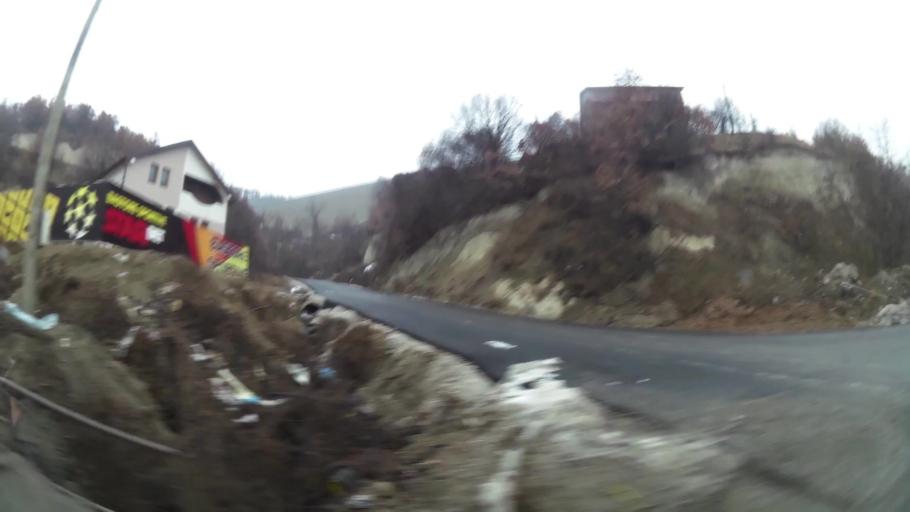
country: XK
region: Ferizaj
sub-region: Hani i Elezit
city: Hani i Elezit
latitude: 42.1565
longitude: 21.2933
